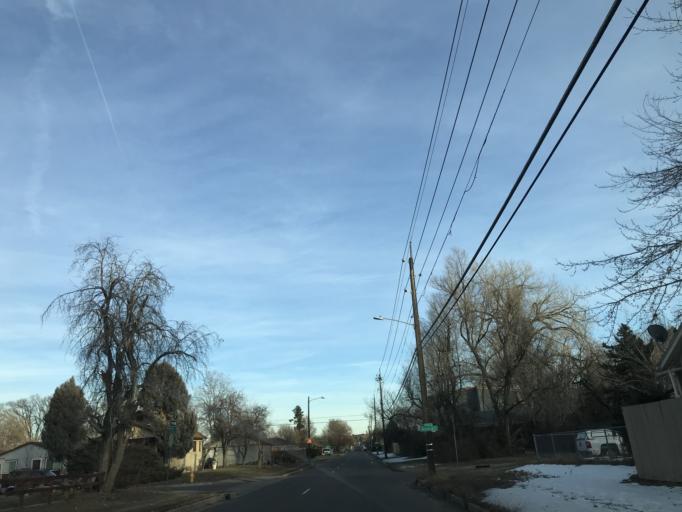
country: US
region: Colorado
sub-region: Arapahoe County
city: Glendale
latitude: 39.7387
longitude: -104.8912
